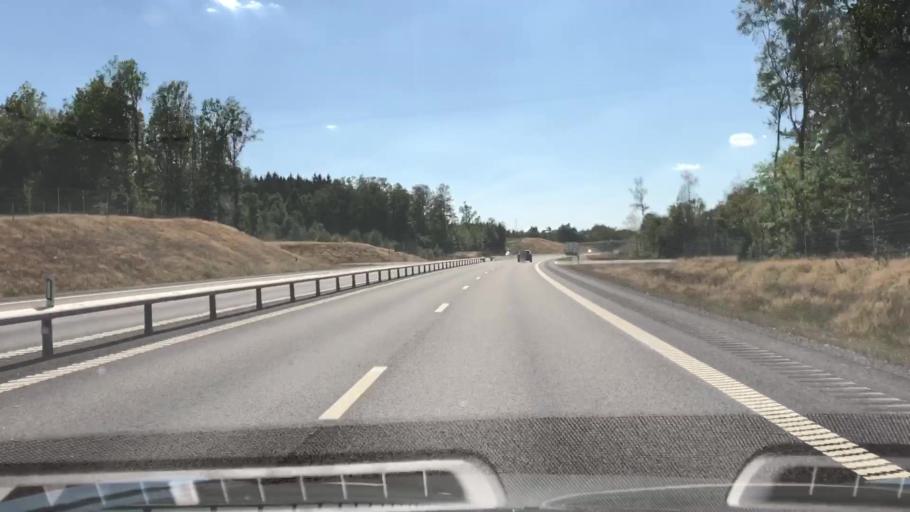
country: SE
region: Skane
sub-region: Hassleholms Kommun
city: Vinslov
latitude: 55.9306
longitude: 13.8433
